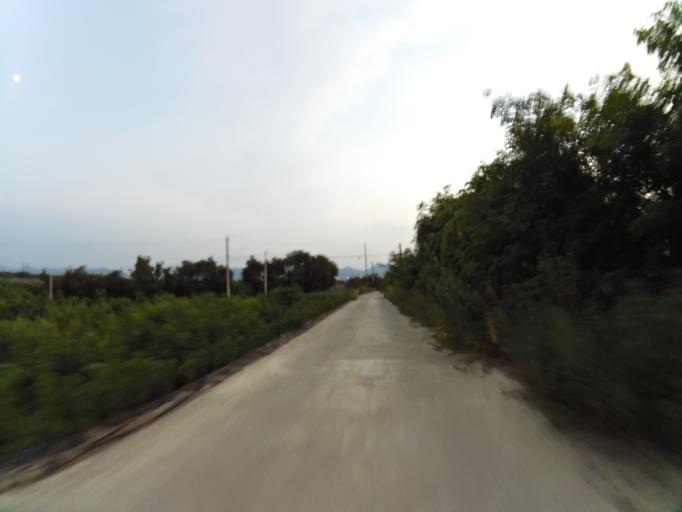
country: KR
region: Gyeongsangbuk-do
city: Gyeongsan-si
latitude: 35.8555
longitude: 128.7454
